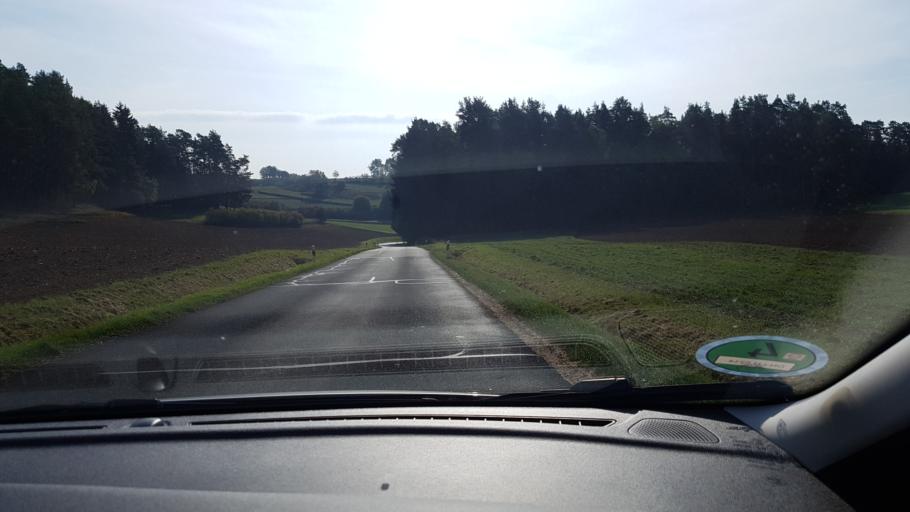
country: DE
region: Bavaria
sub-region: Upper Franconia
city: Waischenfeld
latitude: 49.8203
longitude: 11.3531
